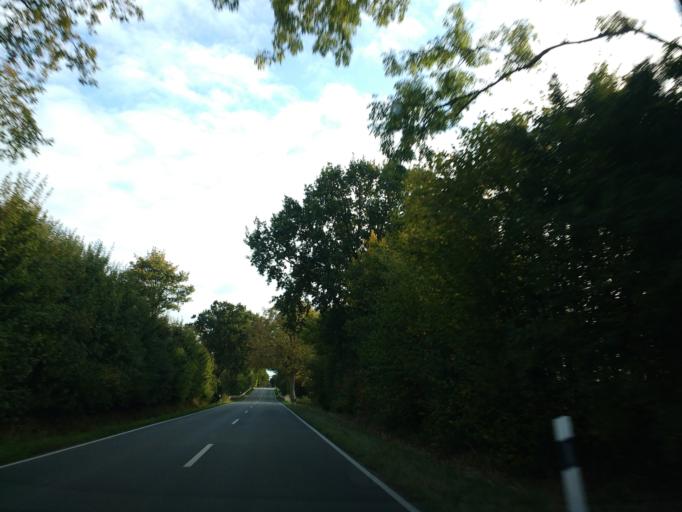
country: DE
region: Schleswig-Holstein
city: Altenkrempe
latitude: 54.1445
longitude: 10.8214
